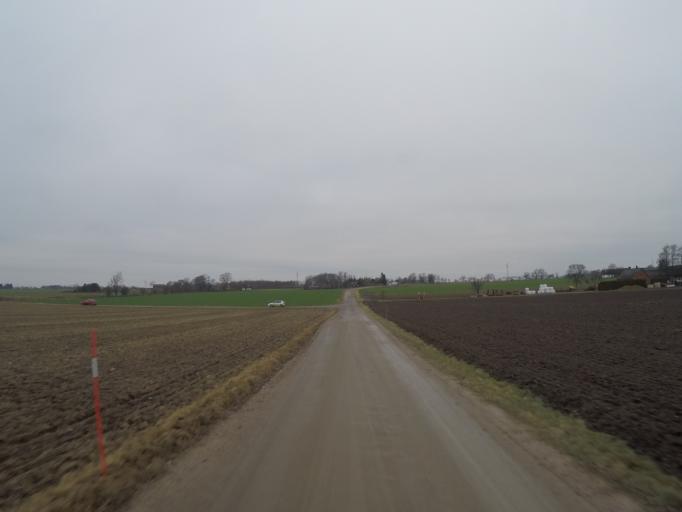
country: SE
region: Skane
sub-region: Hoors Kommun
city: Loberod
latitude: 55.7644
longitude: 13.4479
